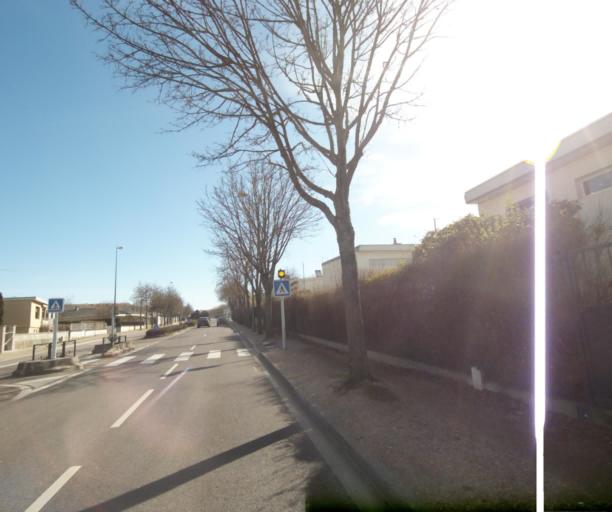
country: FR
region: Lorraine
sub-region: Departement de Meurthe-et-Moselle
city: Villers-les-Nancy
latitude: 48.6714
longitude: 6.1561
